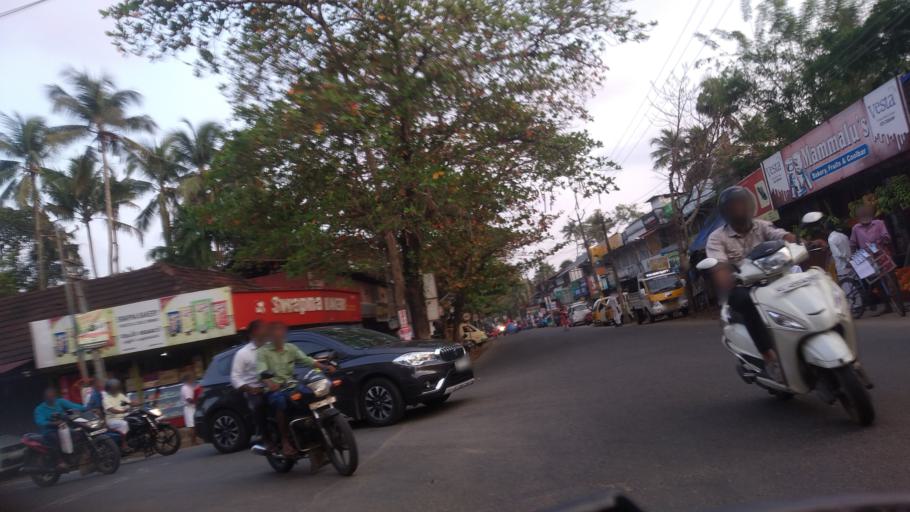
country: IN
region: Kerala
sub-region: Thrissur District
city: Kodungallur
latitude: 10.2235
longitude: 76.1573
